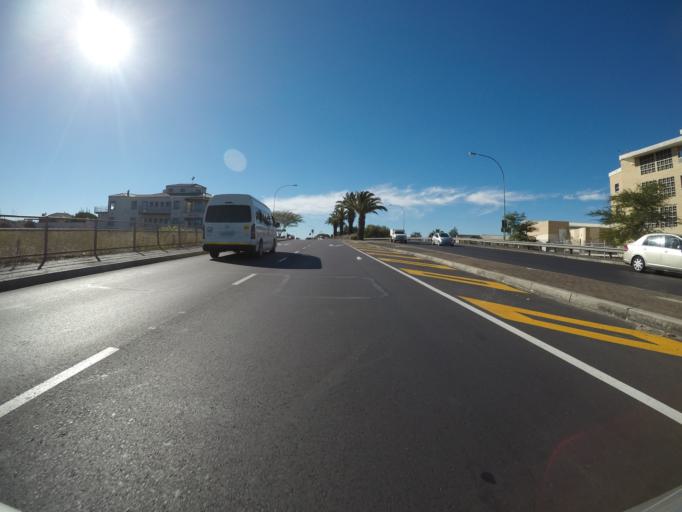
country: ZA
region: Western Cape
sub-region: City of Cape Town
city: Kraaifontein
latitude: -33.9191
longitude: 18.6746
